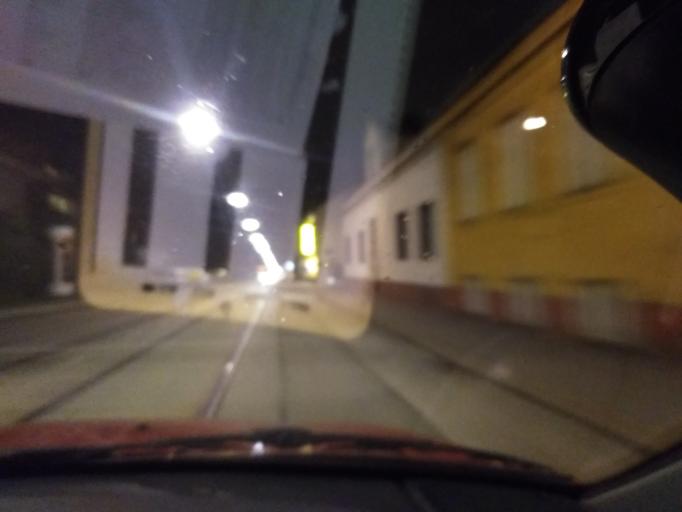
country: AT
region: Lower Austria
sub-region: Politischer Bezirk Modling
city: Perchtoldsdorf
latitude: 48.1655
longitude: 16.2817
